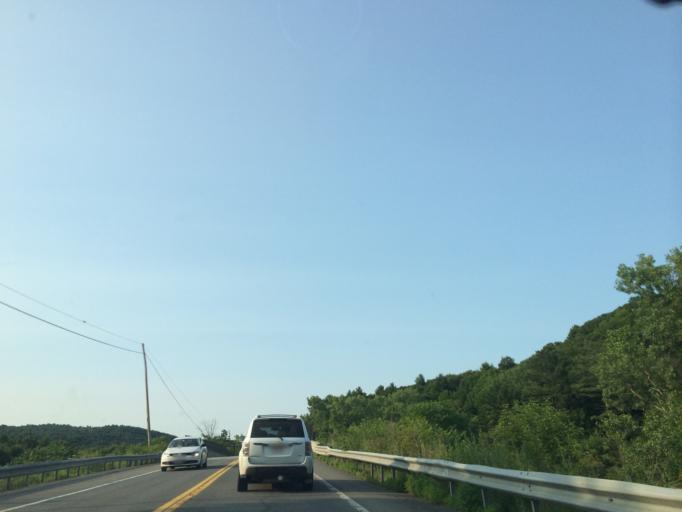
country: US
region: Massachusetts
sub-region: Berkshire County
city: Richmond
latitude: 42.3724
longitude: -73.4303
